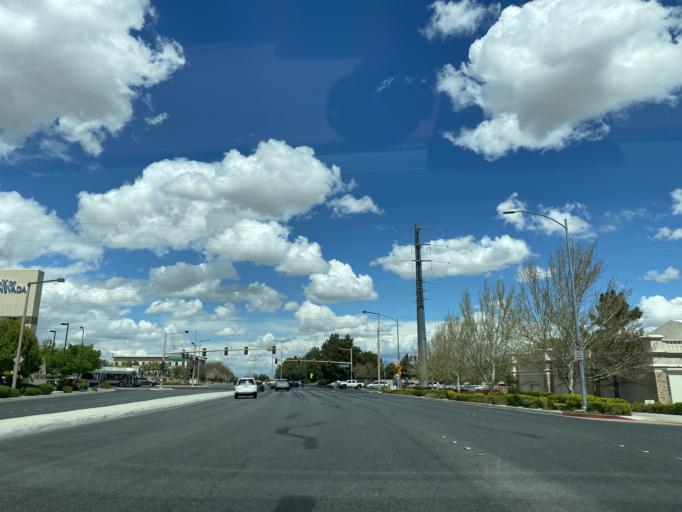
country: US
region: Nevada
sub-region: Clark County
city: Summerlin South
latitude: 36.1579
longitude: -115.3140
